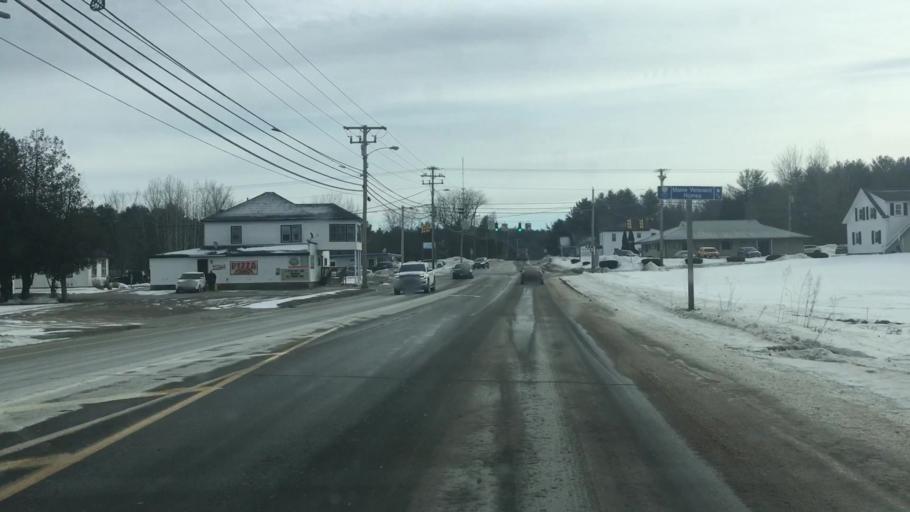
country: US
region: Maine
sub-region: Kennebec County
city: Augusta
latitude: 44.3043
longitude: -69.7437
